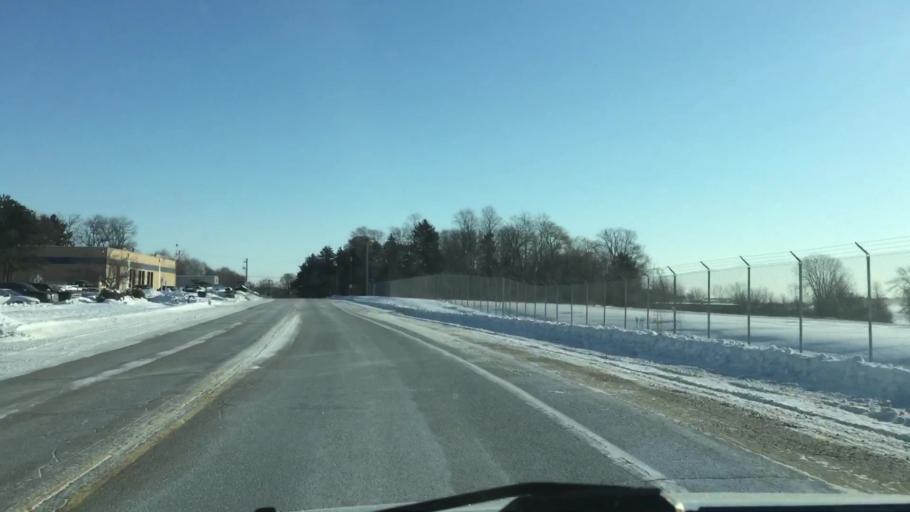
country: US
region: Wisconsin
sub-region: Waukesha County
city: Waukesha
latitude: 43.0446
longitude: -88.2434
